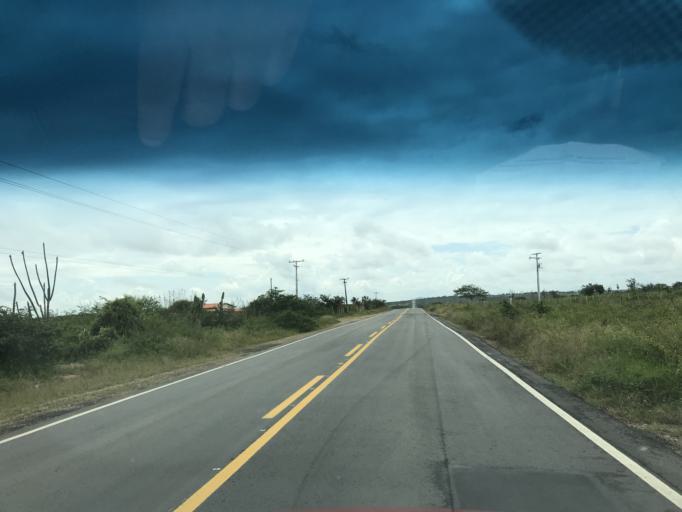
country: BR
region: Bahia
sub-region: Castro Alves
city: Castro Alves
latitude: -12.6818
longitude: -39.3048
